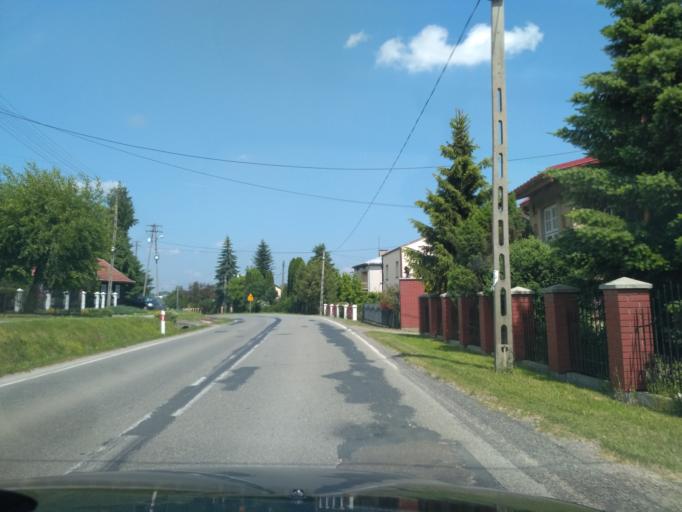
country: PL
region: Subcarpathian Voivodeship
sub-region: Powiat lancucki
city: Albigowa
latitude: 50.0197
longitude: 22.2250
